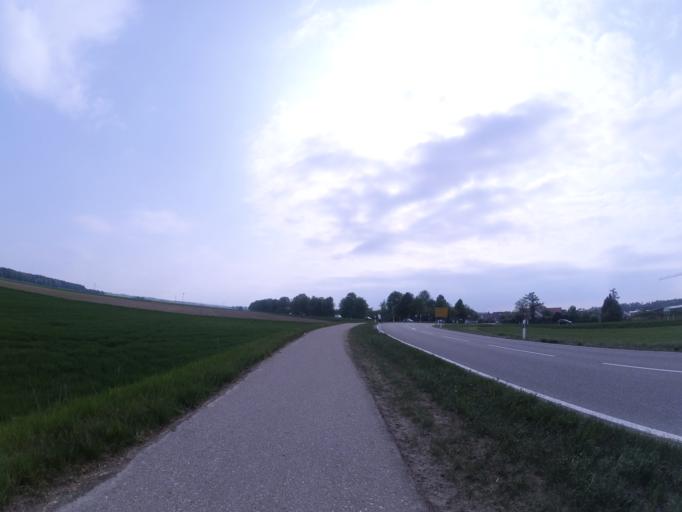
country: DE
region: Baden-Wuerttemberg
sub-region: Tuebingen Region
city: Staig
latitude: 48.3331
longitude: 9.9608
